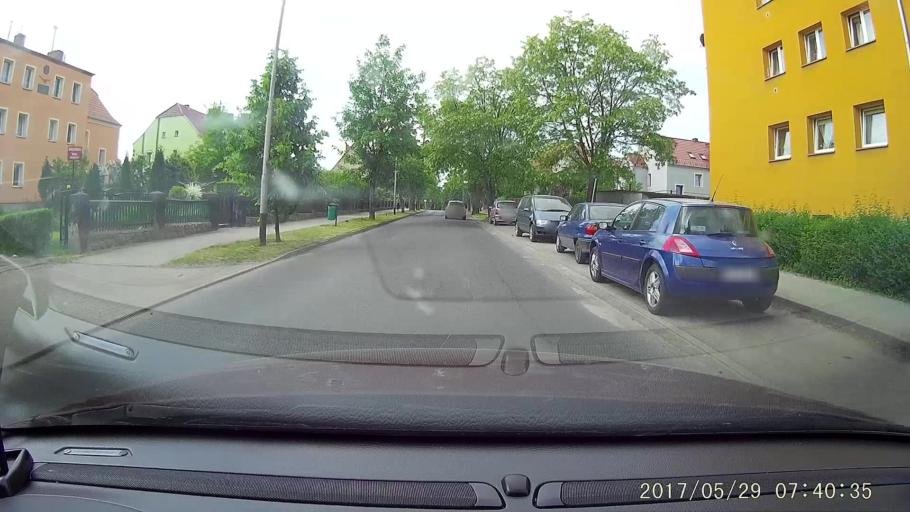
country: PL
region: Lower Silesian Voivodeship
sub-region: Powiat boleslawiecki
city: Boleslawiec
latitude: 51.2613
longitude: 15.5786
